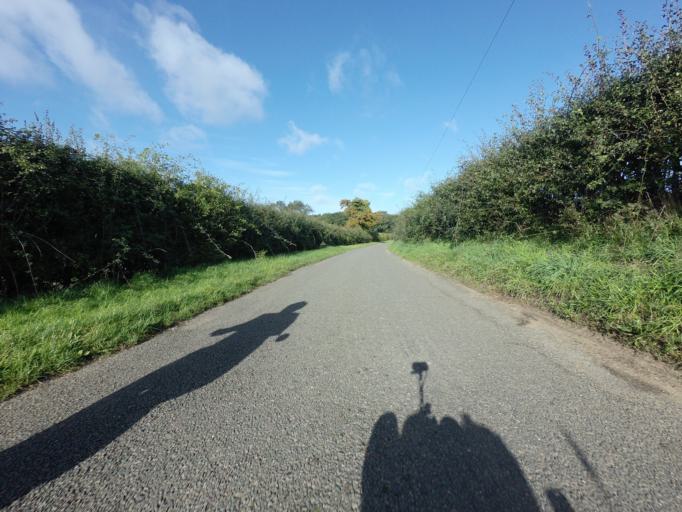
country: GB
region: England
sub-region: Norfolk
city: Dersingham
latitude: 52.8489
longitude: 0.6727
